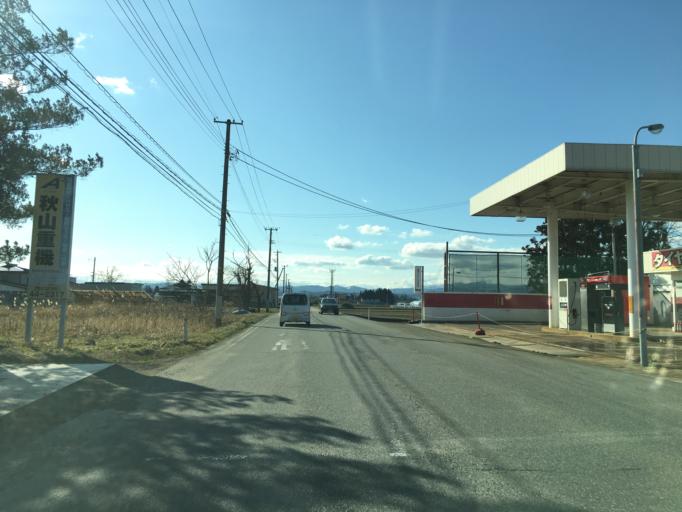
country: JP
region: Yamagata
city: Takahata
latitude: 38.0062
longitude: 140.1029
